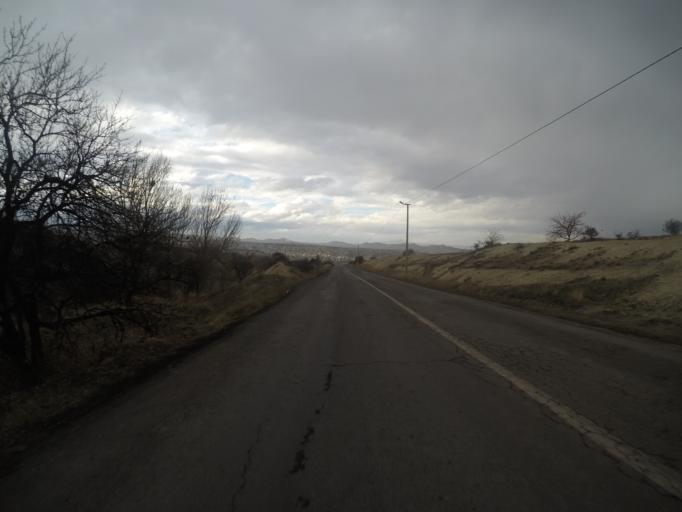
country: TR
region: Nevsehir
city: Goereme
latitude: 38.6385
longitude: 34.8504
